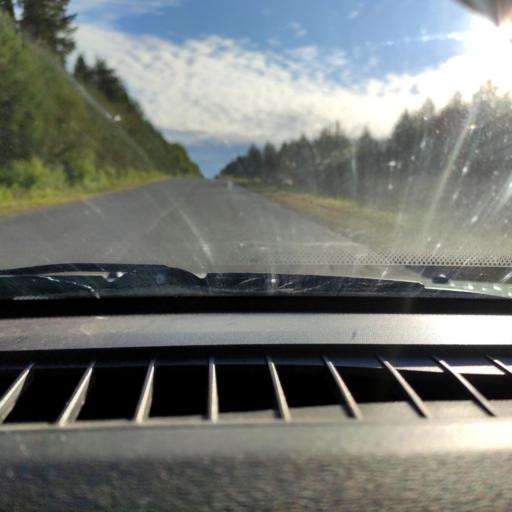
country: RU
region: Perm
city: Uinskoye
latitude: 57.0788
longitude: 56.6110
